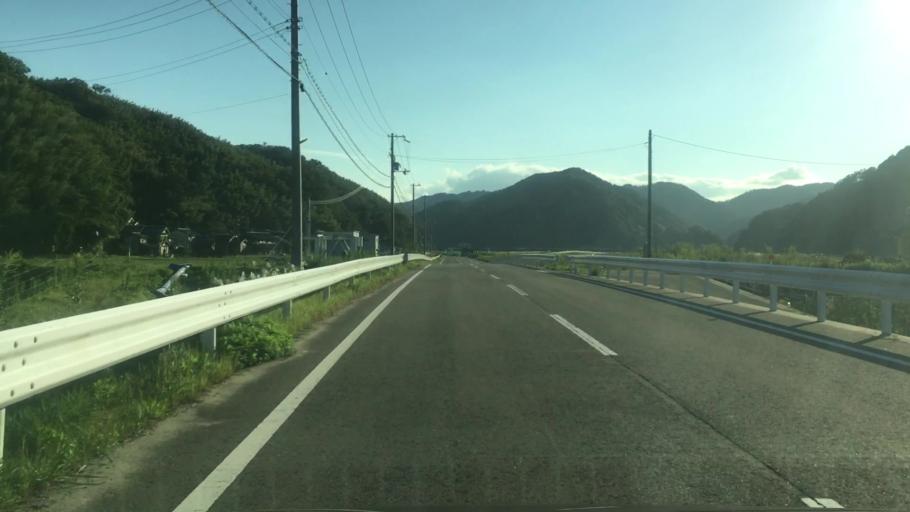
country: JP
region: Hyogo
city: Toyooka
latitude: 35.6156
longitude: 134.8129
